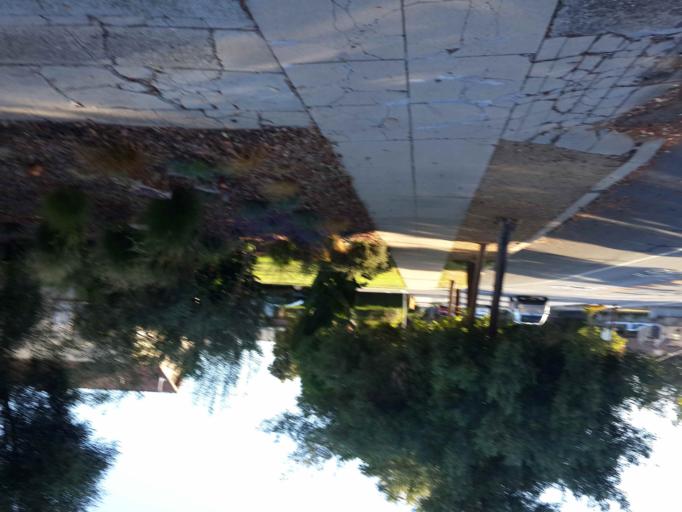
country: US
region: California
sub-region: San Luis Obispo County
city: San Luis Obispo
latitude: 35.2866
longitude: -120.6684
